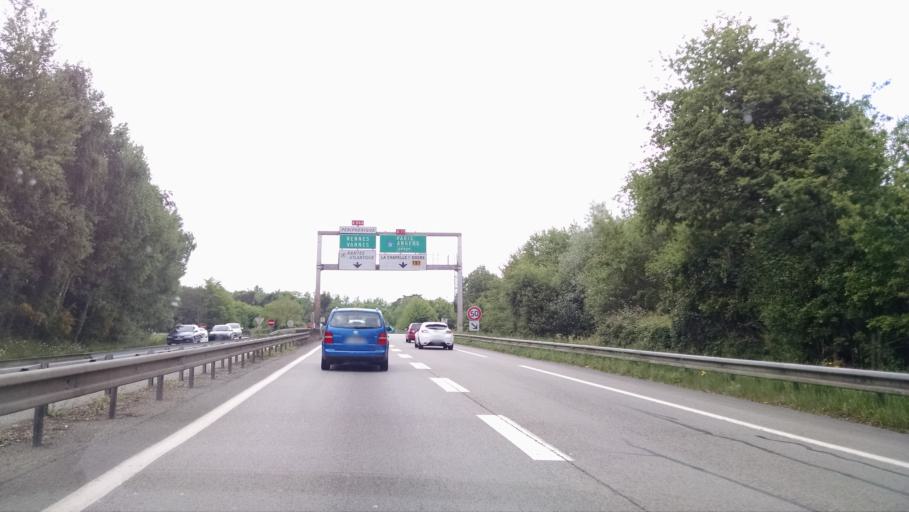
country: FR
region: Pays de la Loire
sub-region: Departement de la Loire-Atlantique
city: La Chapelle-sur-Erdre
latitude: 47.2667
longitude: -1.5605
